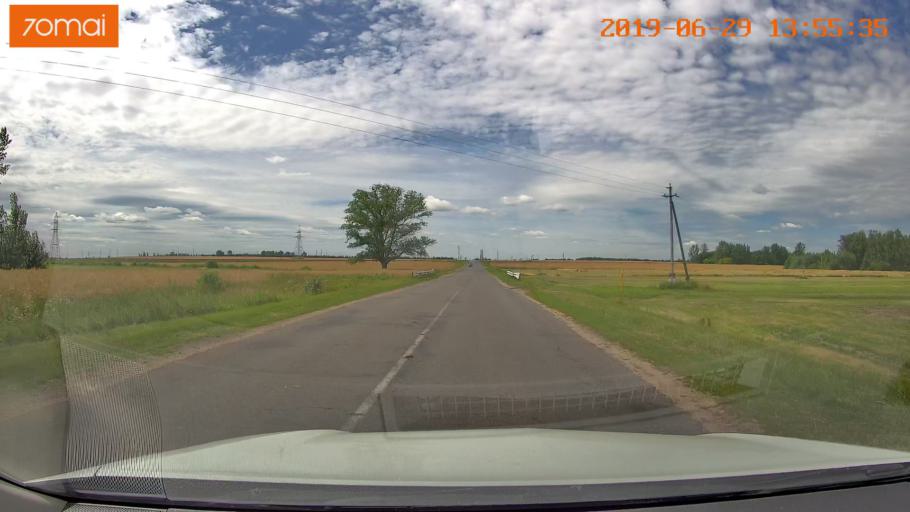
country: BY
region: Minsk
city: Slutsk
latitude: 52.9843
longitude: 27.5171
